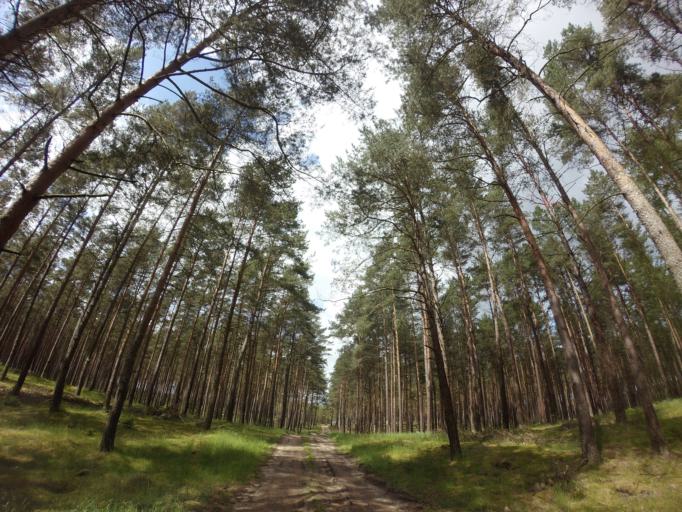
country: PL
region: West Pomeranian Voivodeship
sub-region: Powiat drawski
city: Kalisz Pomorski
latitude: 53.1888
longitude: 15.8975
